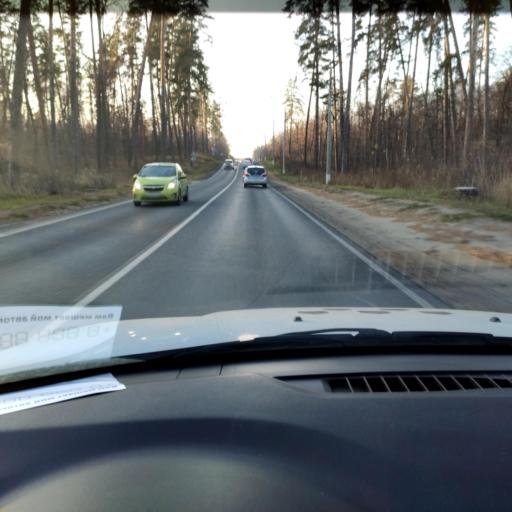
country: RU
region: Samara
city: Tol'yatti
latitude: 53.4916
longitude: 49.3049
